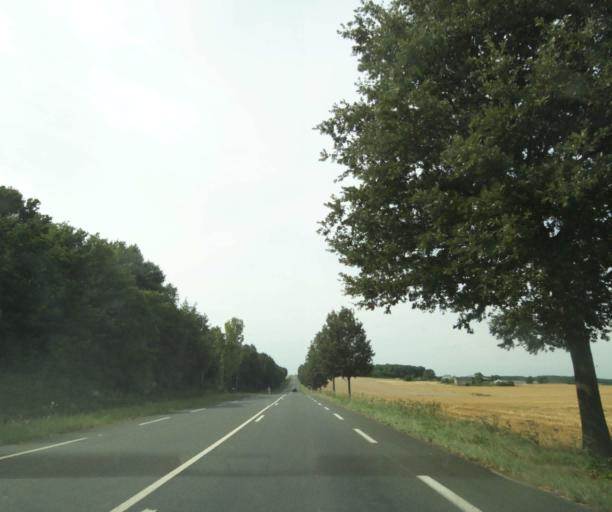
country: FR
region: Centre
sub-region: Departement d'Indre-et-Loire
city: Saint-Christophe-sur-le-Nais
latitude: 47.6470
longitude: 0.4962
